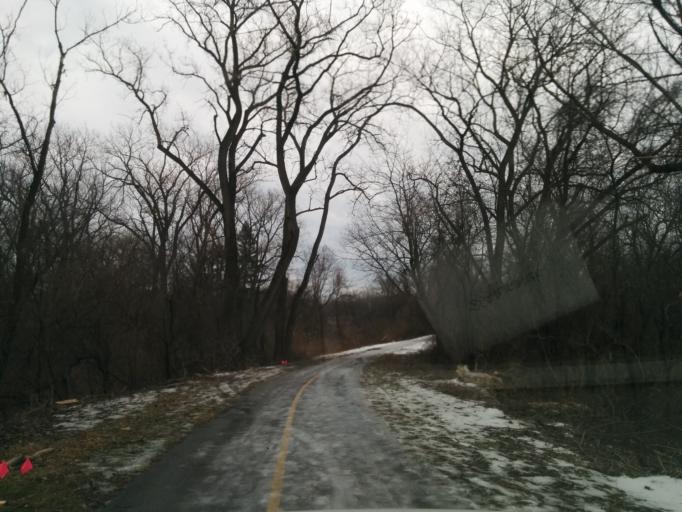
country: US
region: Illinois
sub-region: Cook County
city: Glencoe
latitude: 42.1327
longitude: -87.7791
